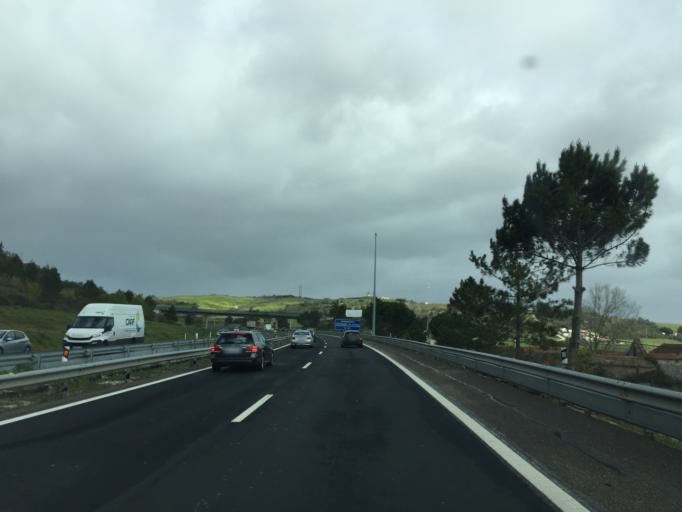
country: PT
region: Lisbon
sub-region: Torres Vedras
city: Torres Vedras
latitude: 39.0853
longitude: -9.2311
